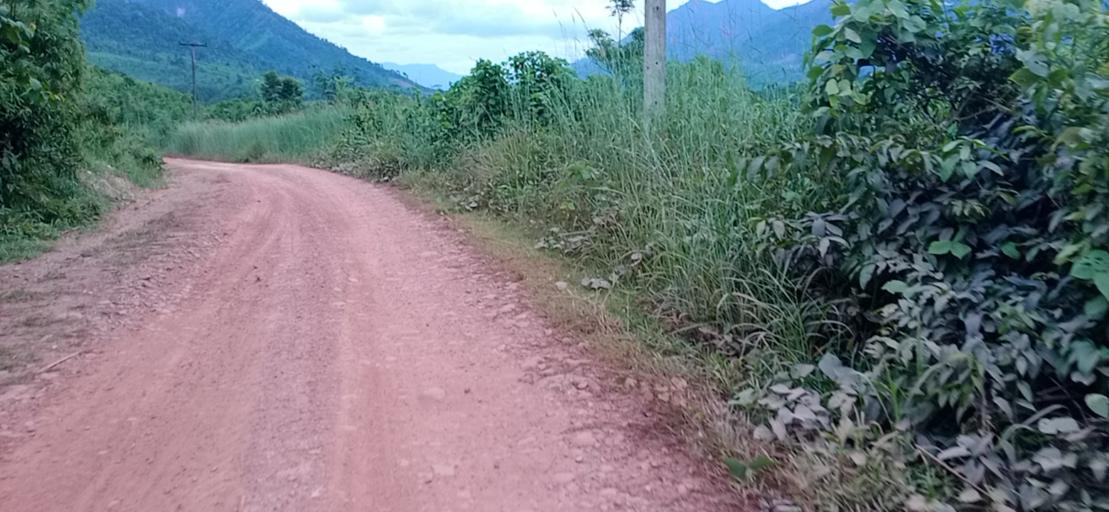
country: TH
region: Changwat Bueng Kan
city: Pak Khat
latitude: 18.5526
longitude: 103.1677
